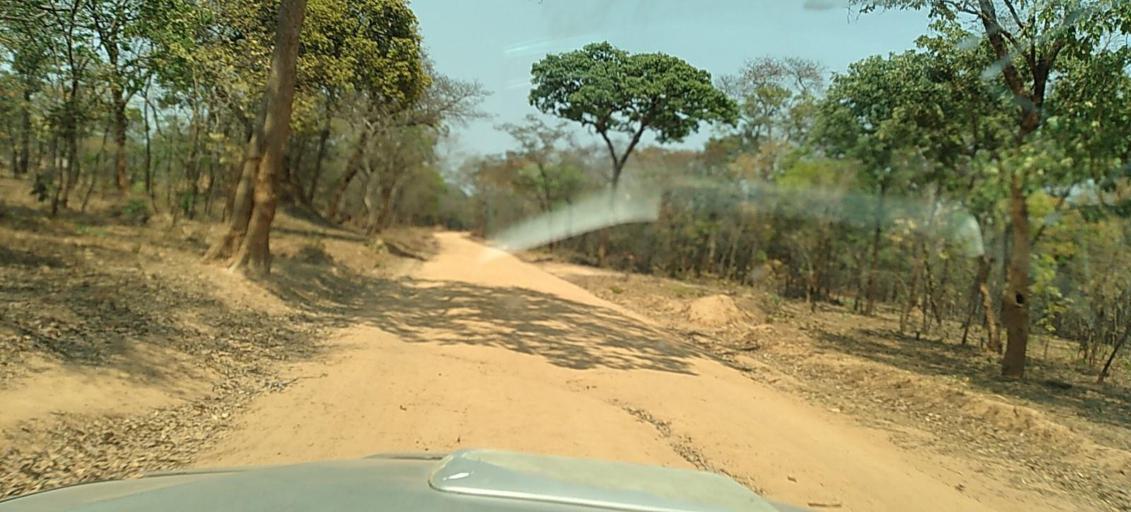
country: ZM
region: North-Western
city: Kasempa
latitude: -13.6645
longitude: 26.2804
